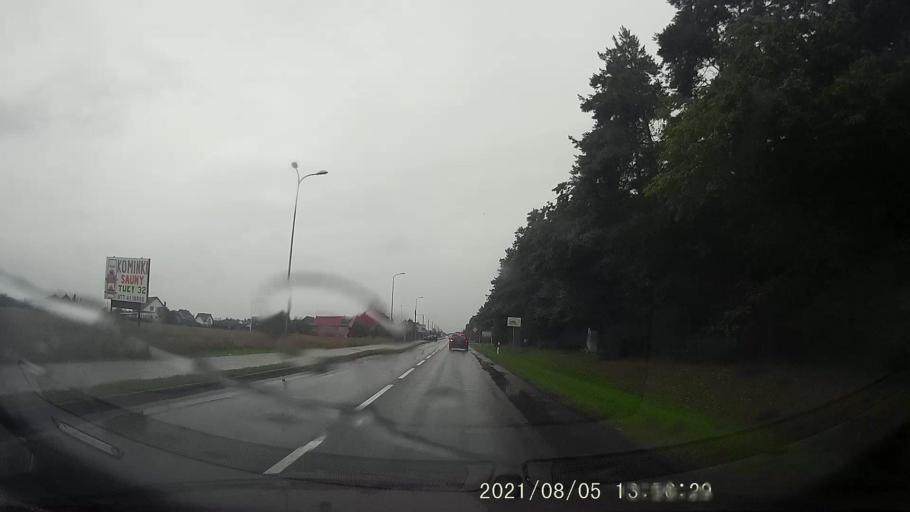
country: PL
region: Opole Voivodeship
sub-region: Powiat krapkowicki
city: Krapkowice
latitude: 50.4631
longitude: 17.9442
